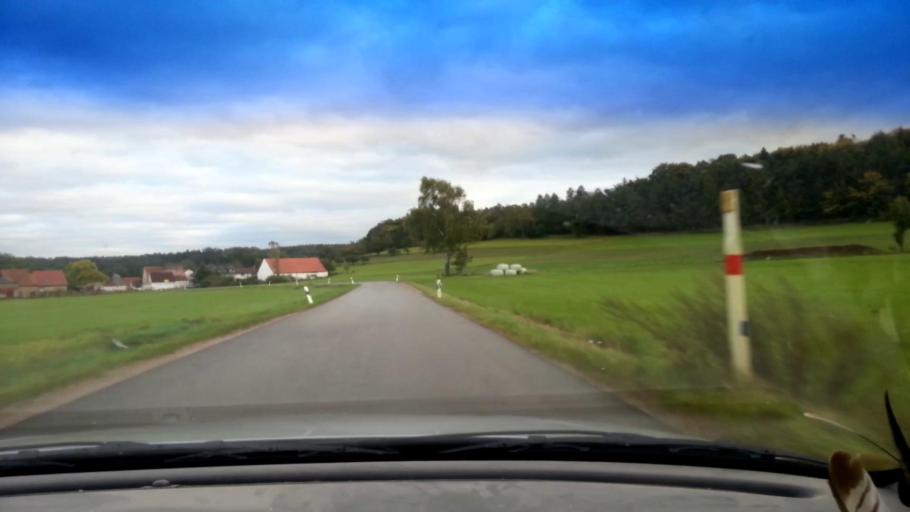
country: DE
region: Bavaria
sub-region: Upper Franconia
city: Burgebrach
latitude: 49.8087
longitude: 10.6967
